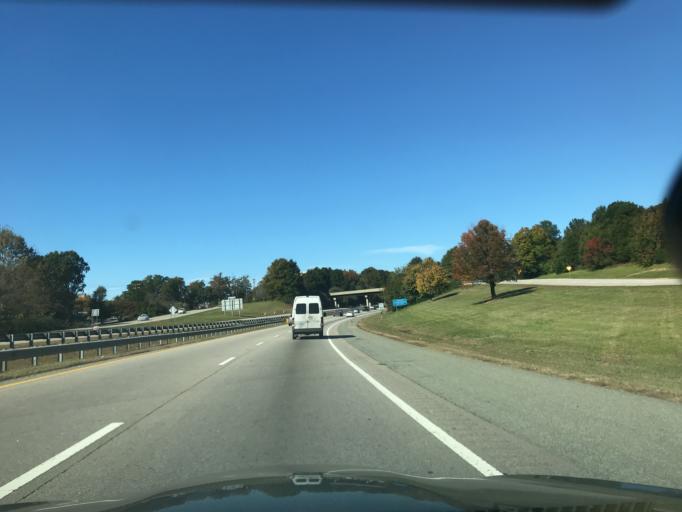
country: US
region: North Carolina
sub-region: Durham County
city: Durham
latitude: 36.0073
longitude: -78.9297
